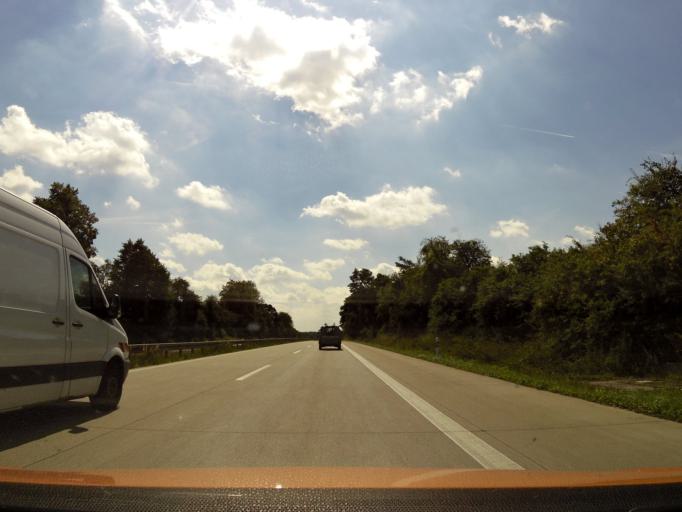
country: DE
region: Brandenburg
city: Althuttendorf
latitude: 53.0819
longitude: 13.8469
